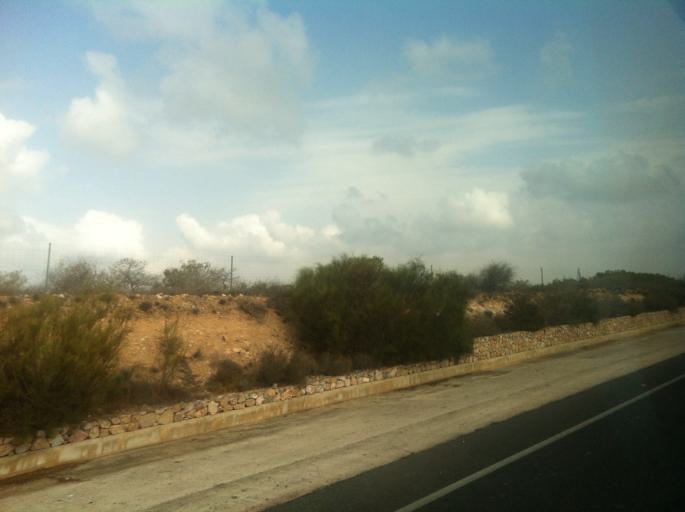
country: ES
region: Valencia
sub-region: Provincia de Alicante
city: Guardamar del Segura
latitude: 38.1384
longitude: -0.6577
